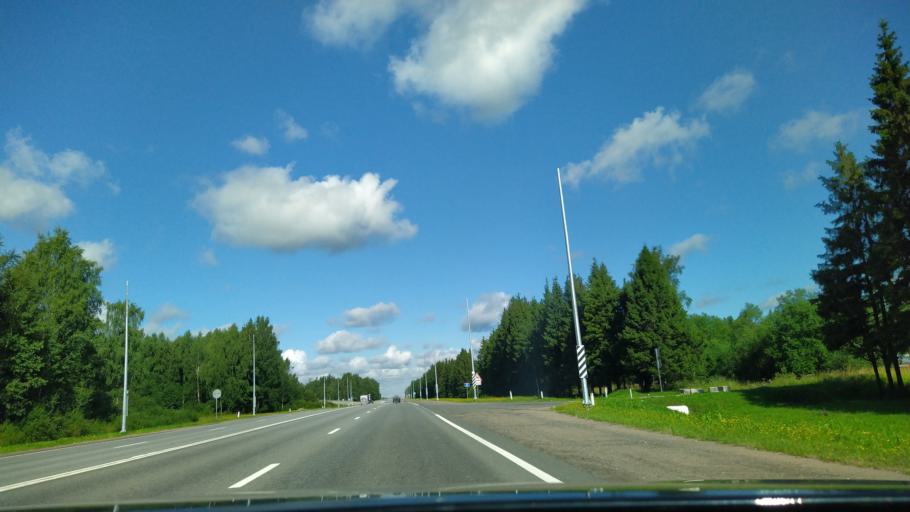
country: RU
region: Leningrad
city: Ul'yanovka
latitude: 59.5893
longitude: 30.7893
